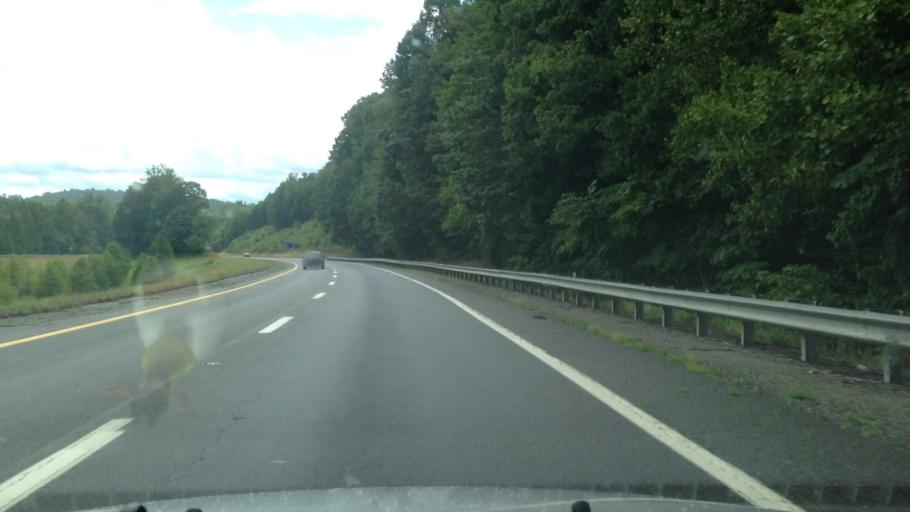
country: US
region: Virginia
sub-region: Henry County
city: Stanleytown
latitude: 36.7062
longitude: -79.9574
